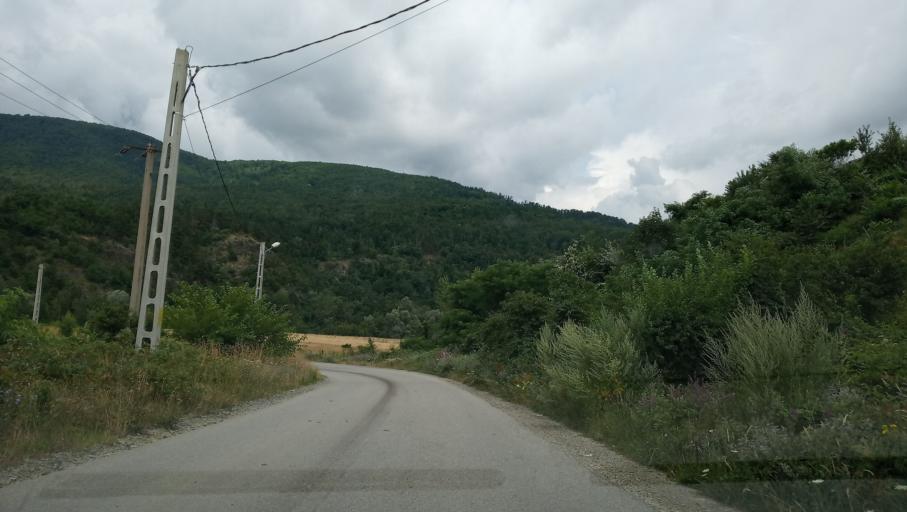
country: RO
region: Gorj
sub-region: Comuna Bumbesti-Jiu
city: Bumbesti-Jiu
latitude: 45.1792
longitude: 23.3748
